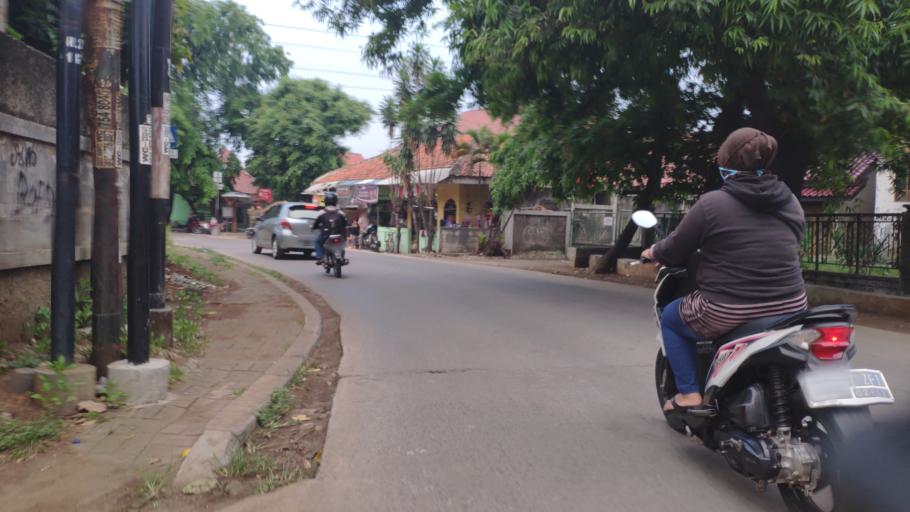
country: ID
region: West Java
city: Pamulang
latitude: -6.3238
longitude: 106.7957
